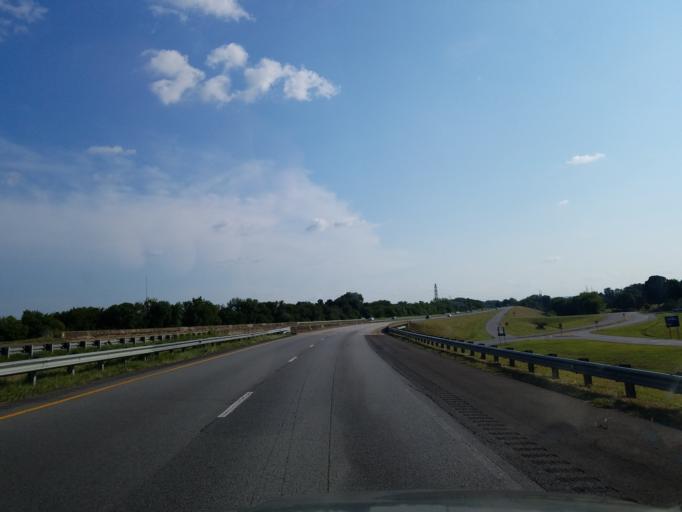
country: US
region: Alabama
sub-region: Jefferson County
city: Brighton
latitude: 33.4287
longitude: -86.9537
